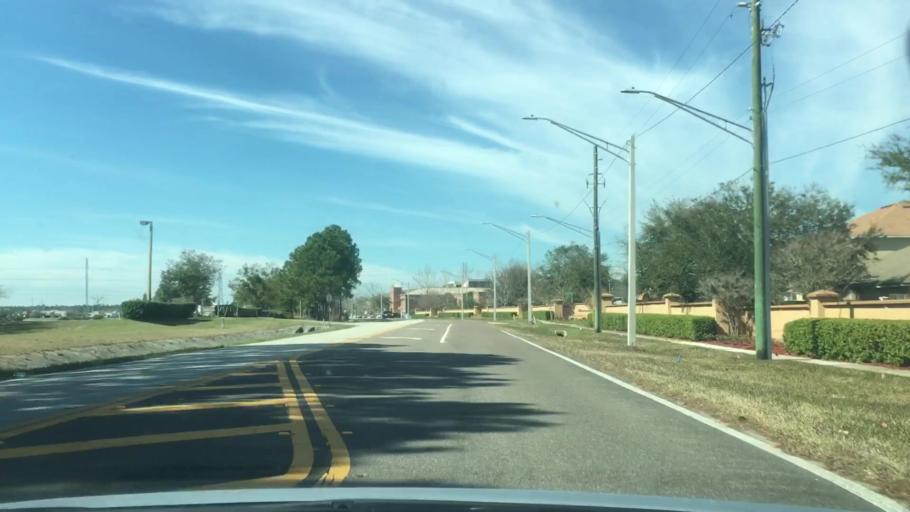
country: US
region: Florida
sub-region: Duval County
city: Atlantic Beach
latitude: 30.3219
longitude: -81.4838
